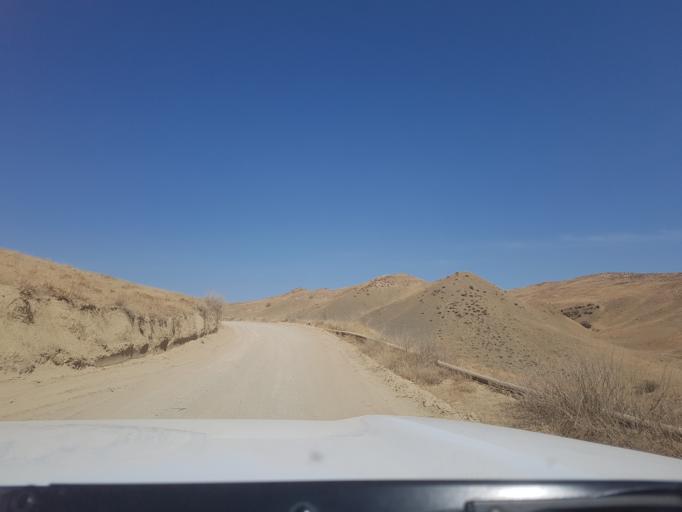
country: TM
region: Ahal
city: Baharly
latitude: 38.2608
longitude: 56.8884
